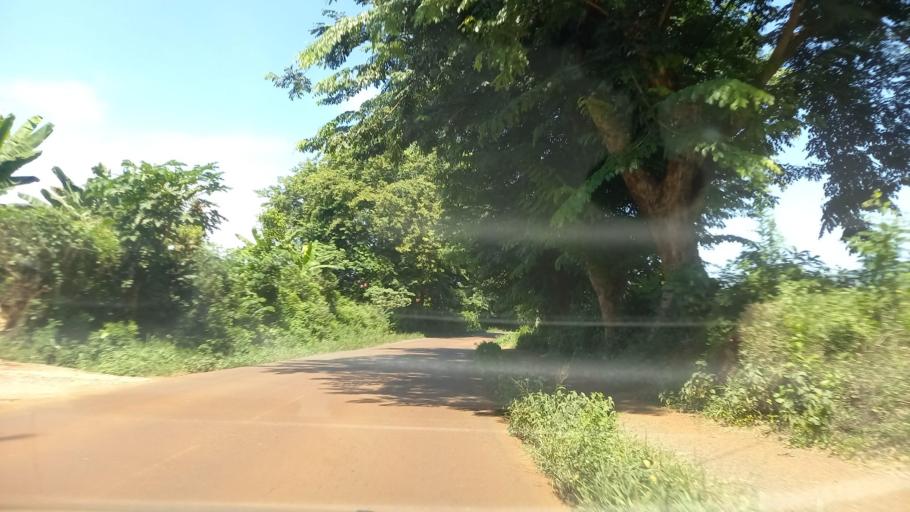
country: YT
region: Tsingoni
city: Tsingoni
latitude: -12.7927
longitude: 45.1168
